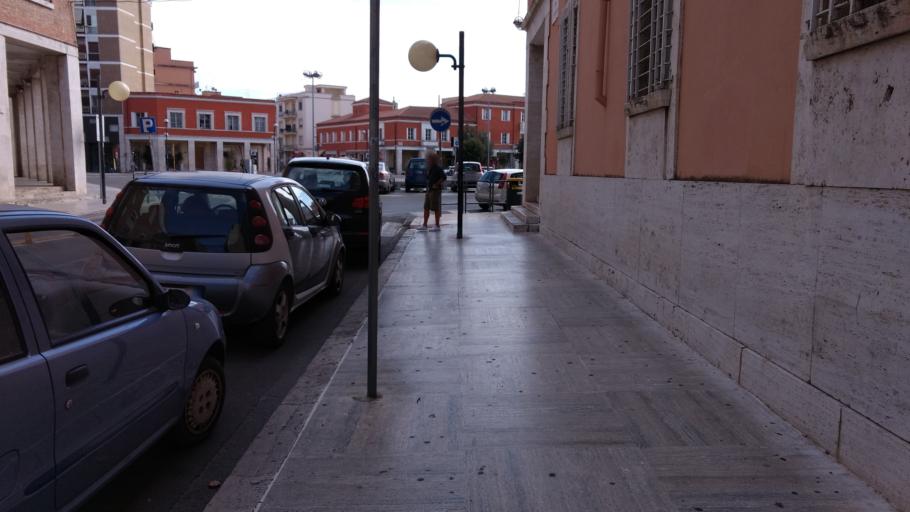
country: IT
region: Latium
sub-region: Provincia di Latina
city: Latina
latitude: 41.4679
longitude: 12.9042
